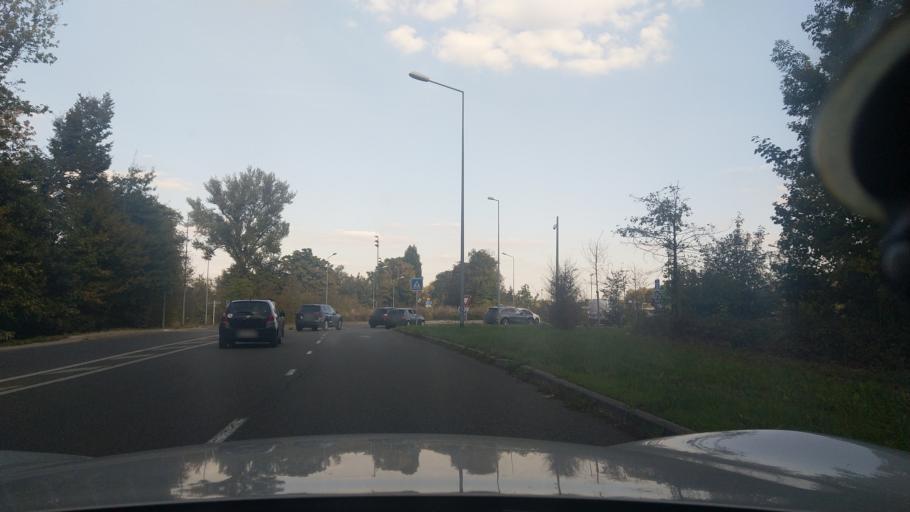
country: FR
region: Ile-de-France
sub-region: Departement des Hauts-de-Seine
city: Vaucresson
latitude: 48.8331
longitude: 2.1452
